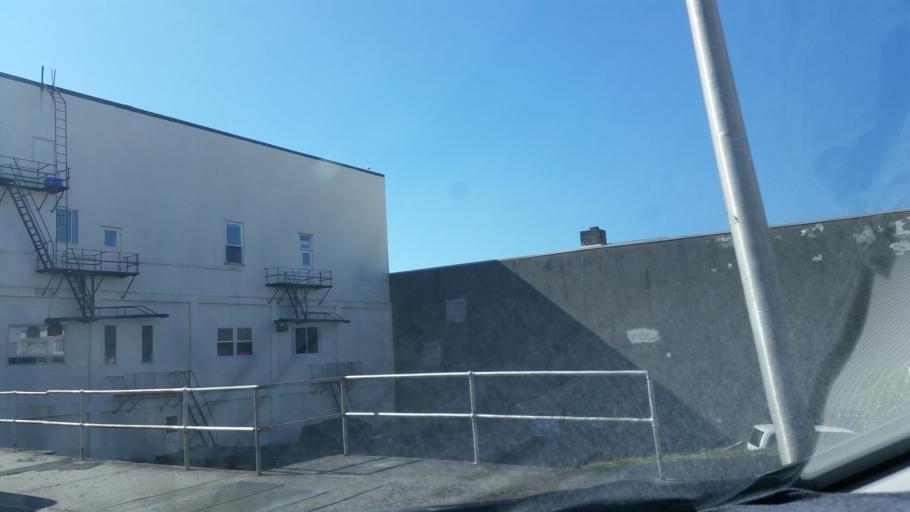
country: US
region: Oregon
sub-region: Clatsop County
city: Astoria
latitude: 46.1884
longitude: -123.8328
